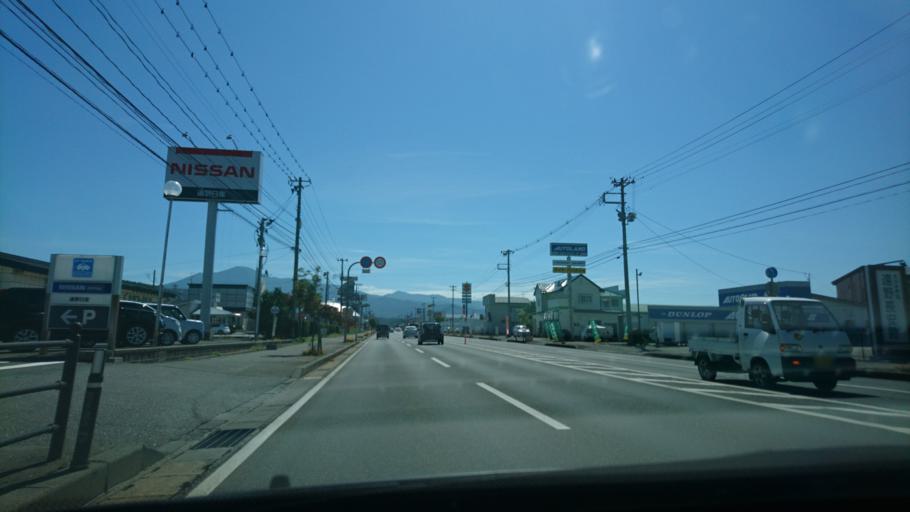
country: JP
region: Iwate
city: Tono
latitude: 39.3369
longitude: 141.5454
